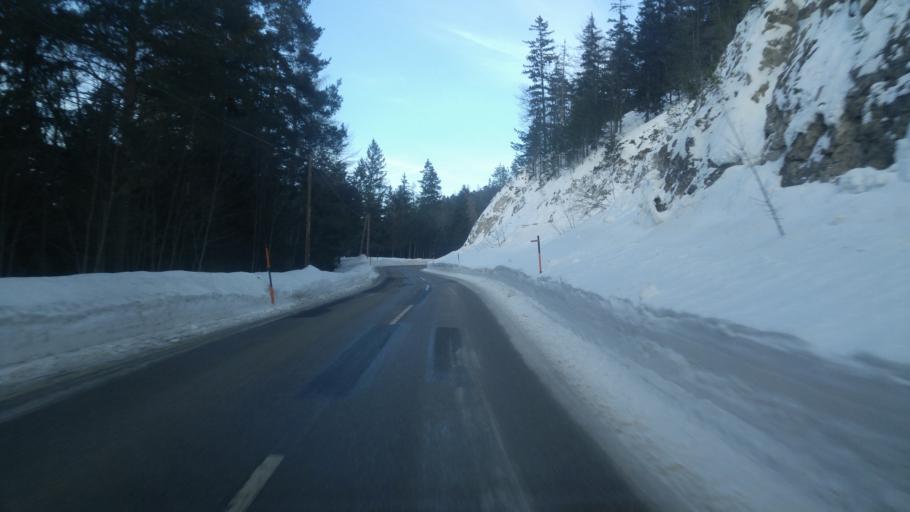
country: AT
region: Lower Austria
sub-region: Politischer Bezirk Lilienfeld
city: Hohenberg
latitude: 47.8790
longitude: 15.6352
